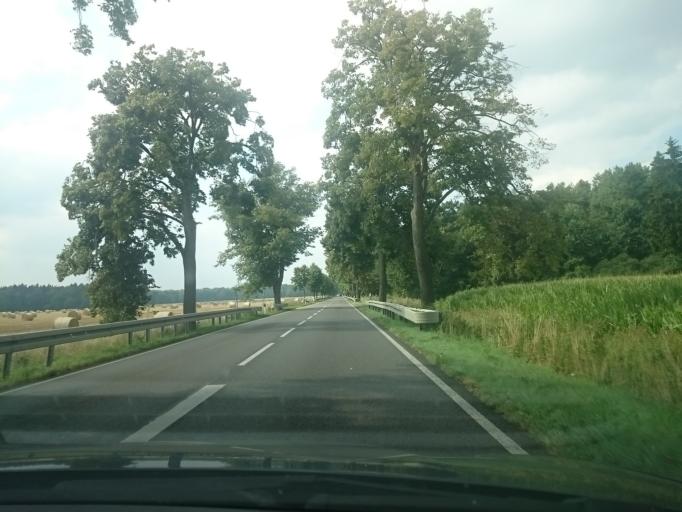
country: DE
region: Mecklenburg-Vorpommern
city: Ducherow
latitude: 53.7244
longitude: 13.8172
